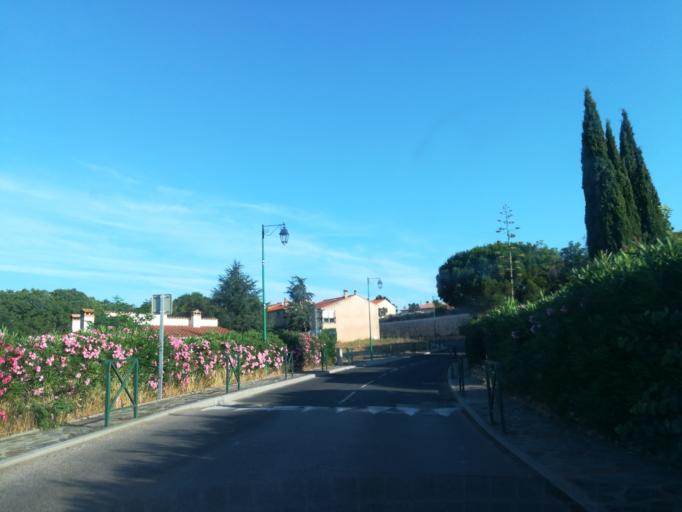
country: FR
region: Languedoc-Roussillon
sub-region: Departement des Pyrenees-Orientales
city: Sant Joan de Pladecorts
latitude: 42.5121
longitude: 2.7891
